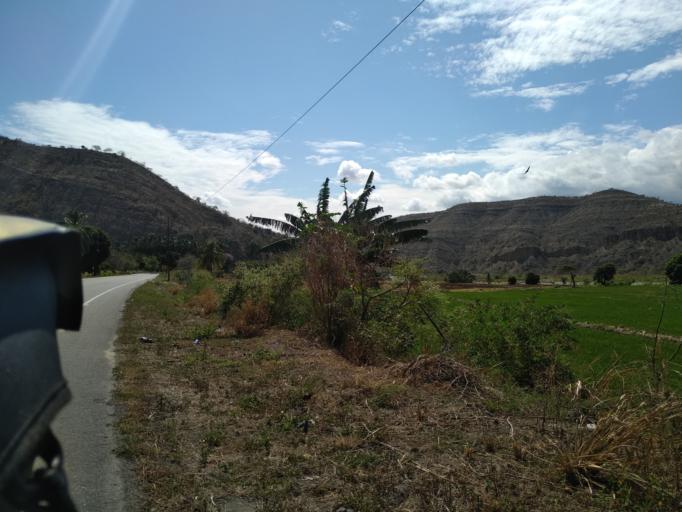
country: PE
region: Cajamarca
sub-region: Provincia de Cutervo
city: Choros
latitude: -5.8195
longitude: -78.7423
